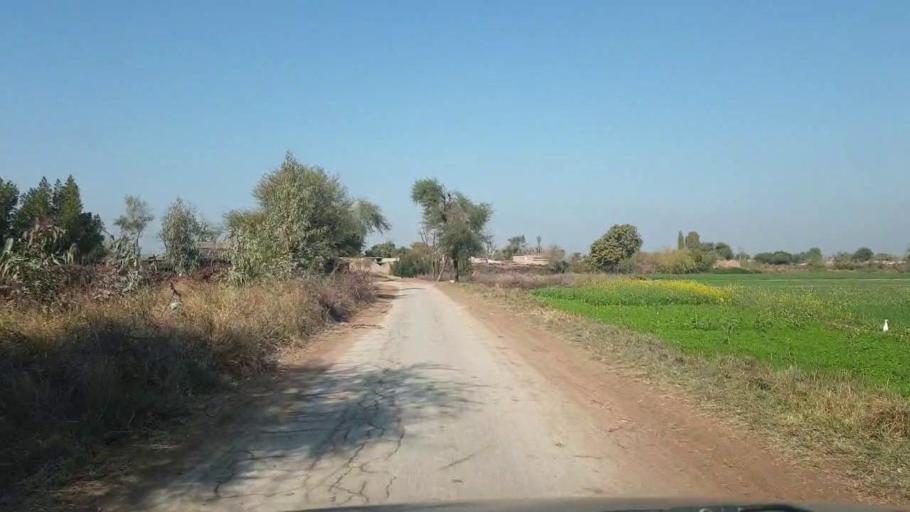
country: PK
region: Sindh
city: Shahdadpur
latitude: 25.8867
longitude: 68.5416
